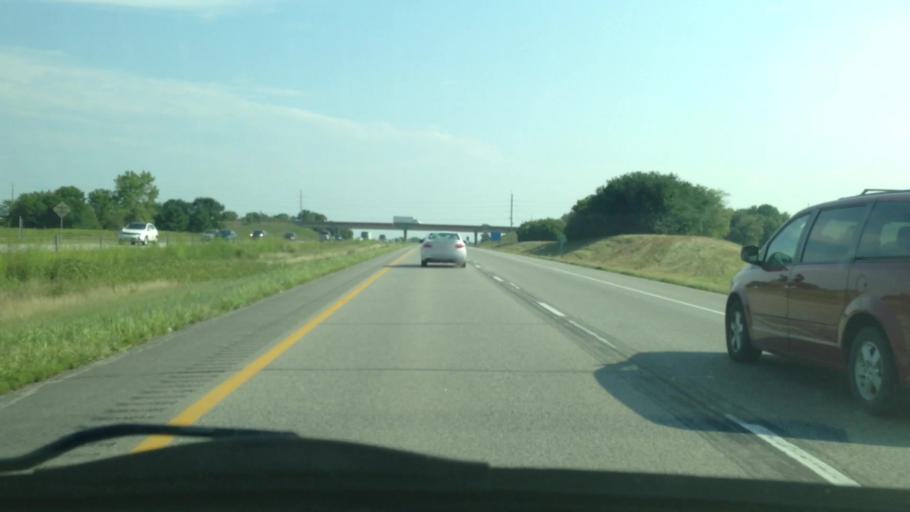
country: US
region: Iowa
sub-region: Linn County
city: Ely
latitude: 41.8940
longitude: -91.6713
